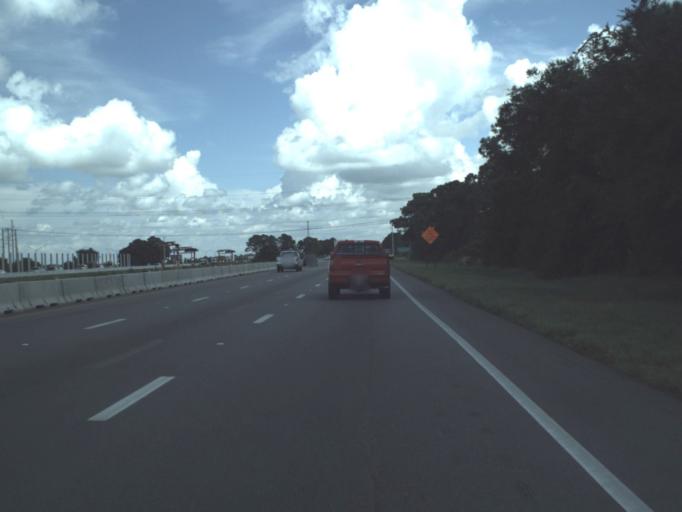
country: US
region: Florida
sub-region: Sarasota County
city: The Meadows
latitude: 27.3541
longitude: -82.4461
